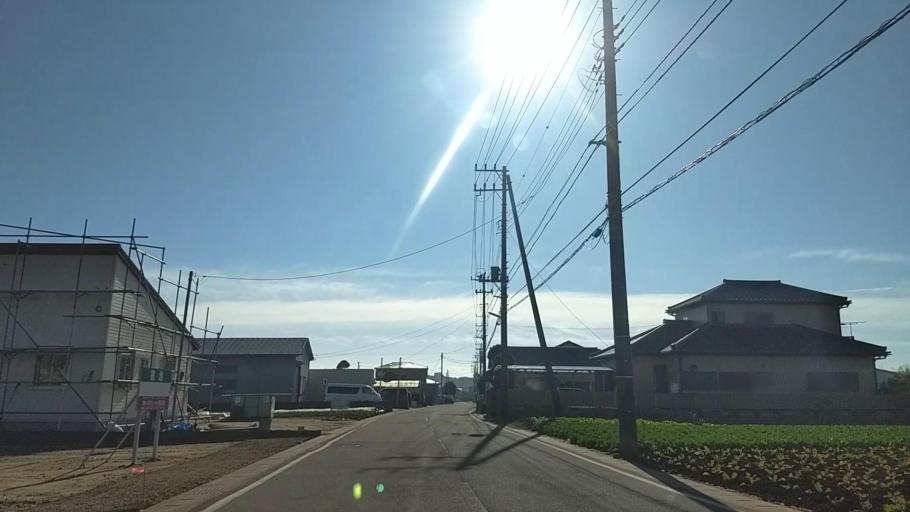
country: JP
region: Chiba
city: Hasaki
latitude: 35.7217
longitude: 140.8440
